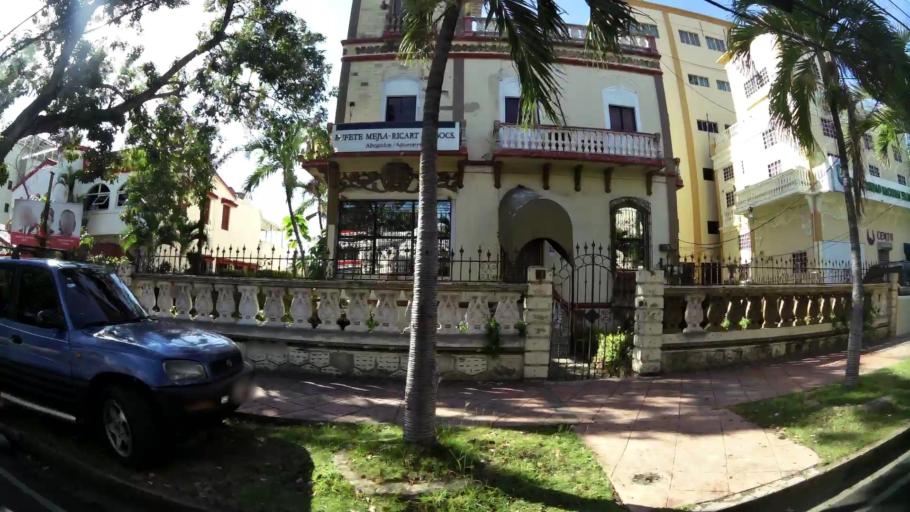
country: DO
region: Nacional
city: Ciudad Nueva
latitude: 18.4706
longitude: -69.8972
